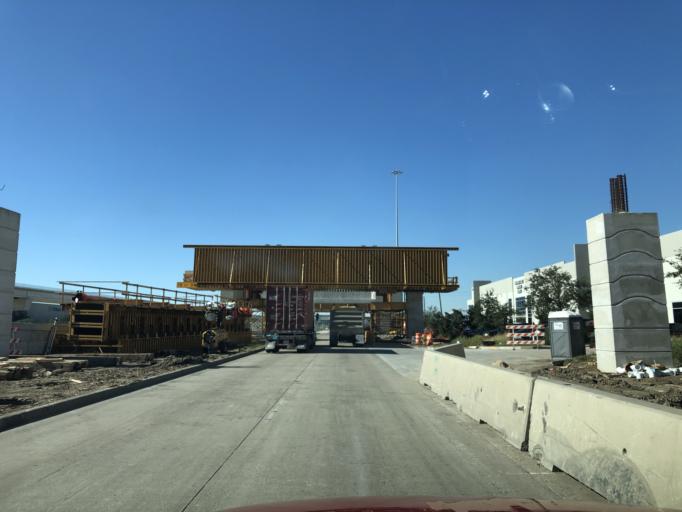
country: US
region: Texas
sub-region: Brazoria County
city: Brookside Village
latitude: 29.5984
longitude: -95.3711
